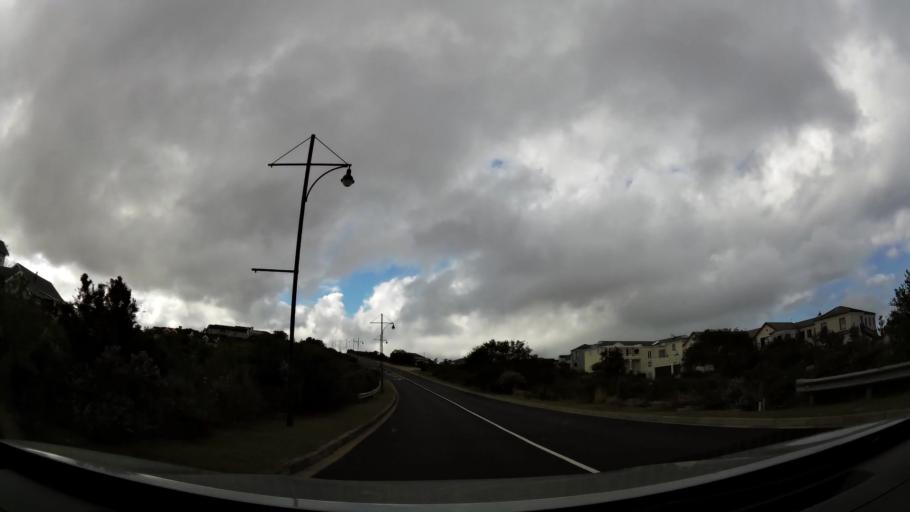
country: ZA
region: Western Cape
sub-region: Eden District Municipality
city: Knysna
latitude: -34.0673
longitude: 23.0973
